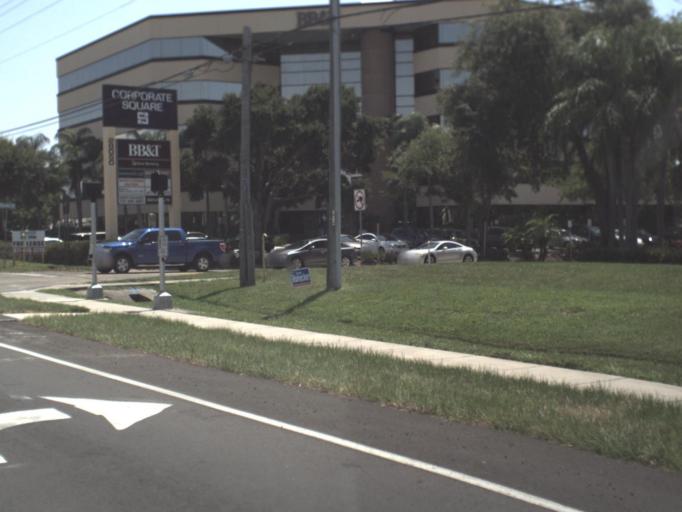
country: US
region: Florida
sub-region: Pinellas County
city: Saint George
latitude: 28.0280
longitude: -82.7383
